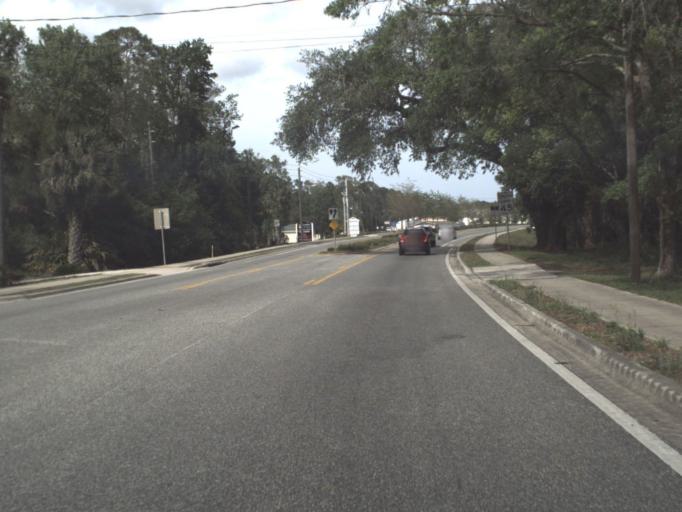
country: US
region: Florida
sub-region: Flagler County
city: Bunnell
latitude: 29.4722
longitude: -81.2516
